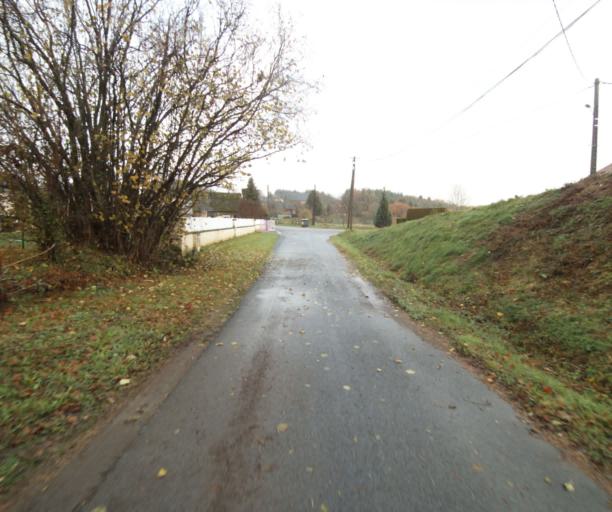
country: FR
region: Limousin
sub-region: Departement de la Correze
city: Cornil
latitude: 45.1909
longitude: 1.6447
